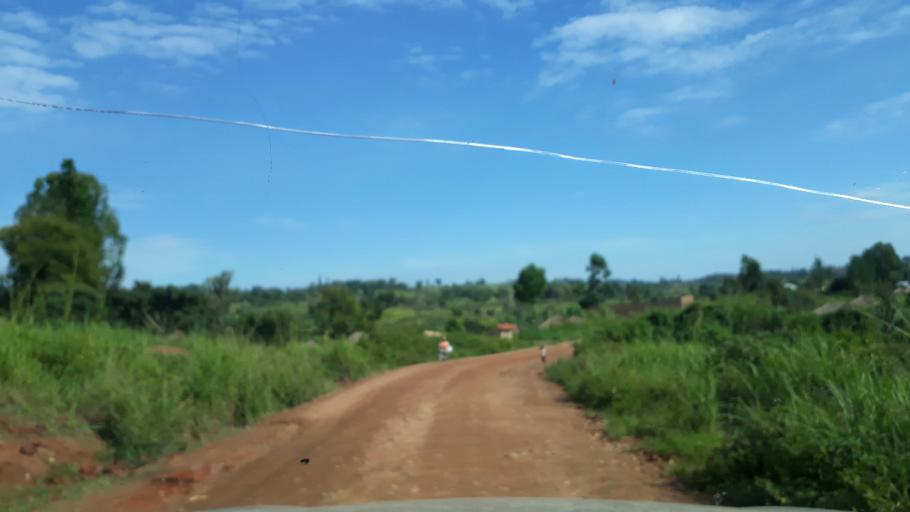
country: UG
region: Northern Region
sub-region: Zombo District
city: Paidha
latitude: 2.3663
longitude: 31.0276
